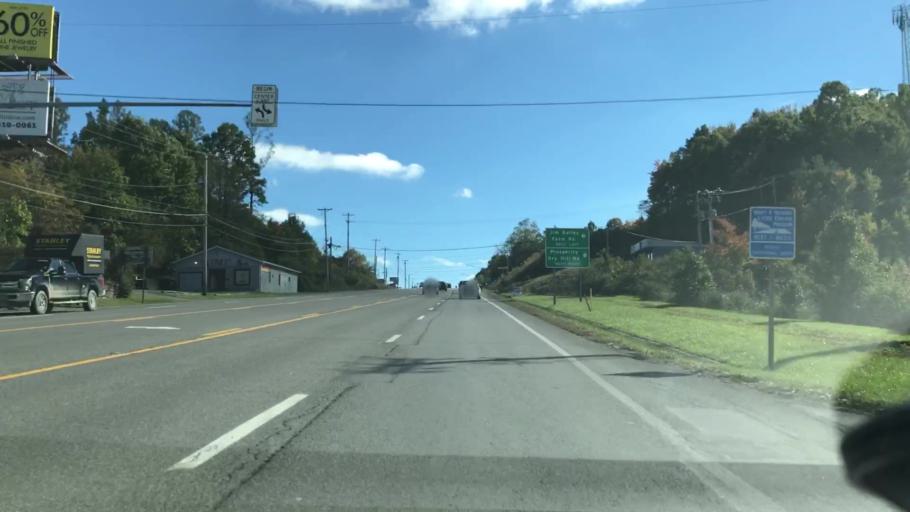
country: US
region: West Virginia
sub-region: Raleigh County
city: Prosperity
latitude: 37.8459
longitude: -81.1950
